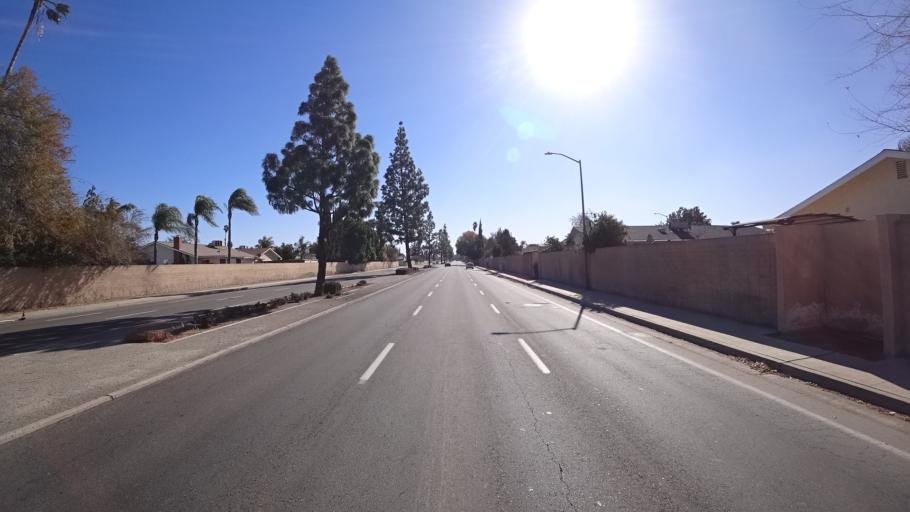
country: US
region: California
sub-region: Kern County
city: Bakersfield
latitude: 35.3369
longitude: -119.0603
